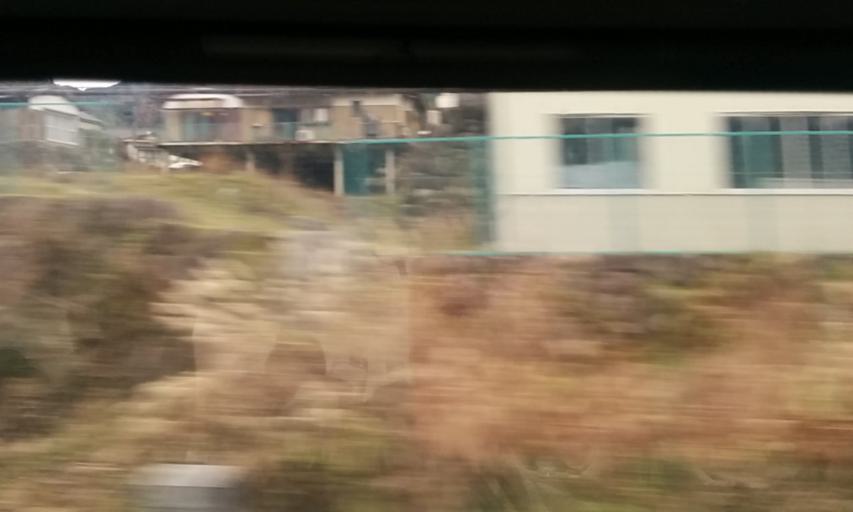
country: JP
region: Gifu
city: Nakatsugawa
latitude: 35.6049
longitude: 137.6092
